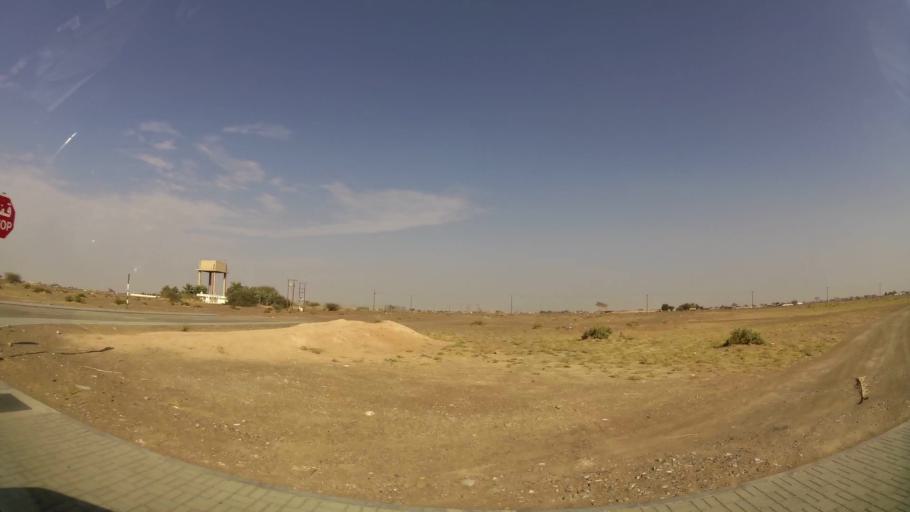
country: AE
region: Abu Dhabi
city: Al Ain
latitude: 24.0383
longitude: 55.8539
